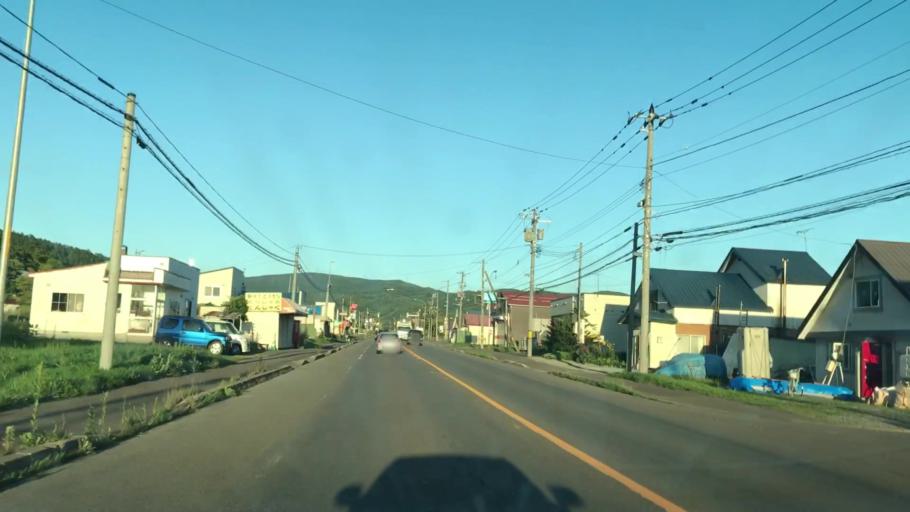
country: JP
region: Hokkaido
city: Niseko Town
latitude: 42.7974
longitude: 140.9458
